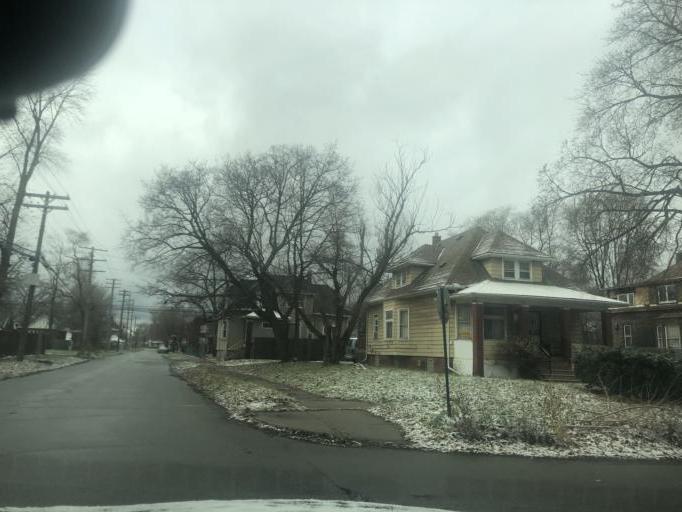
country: US
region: Michigan
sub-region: Wayne County
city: River Rouge
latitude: 42.3106
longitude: -83.1110
